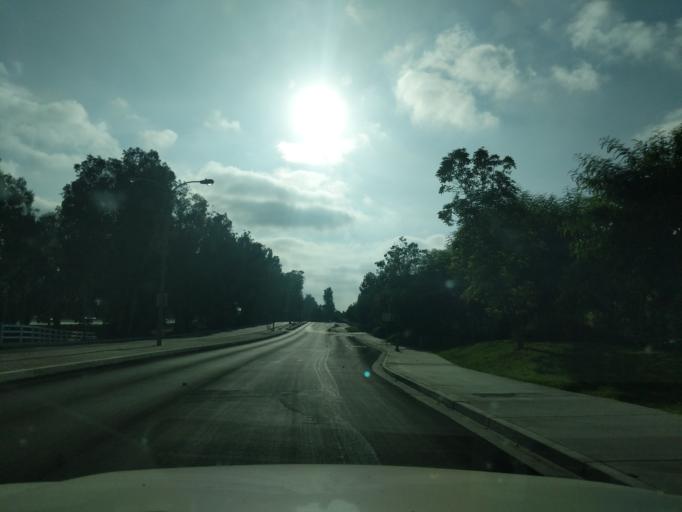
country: US
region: California
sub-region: Ventura County
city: Camarillo
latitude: 34.2164
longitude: -119.0163
